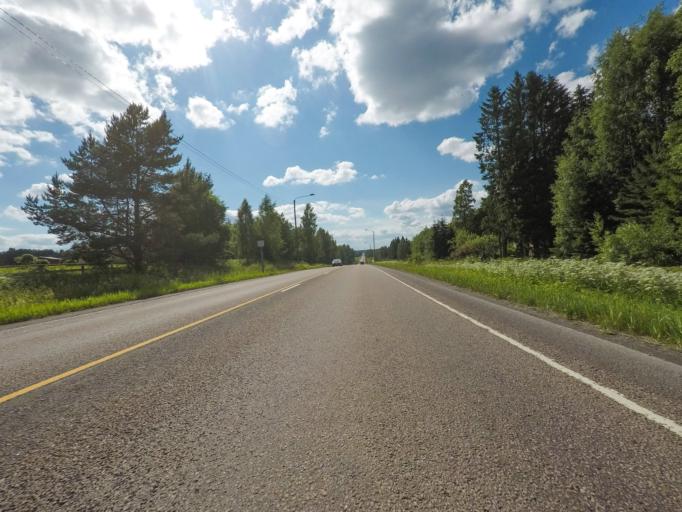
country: FI
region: Southern Savonia
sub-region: Savonlinna
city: Kerimaeki
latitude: 61.8835
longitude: 29.0839
